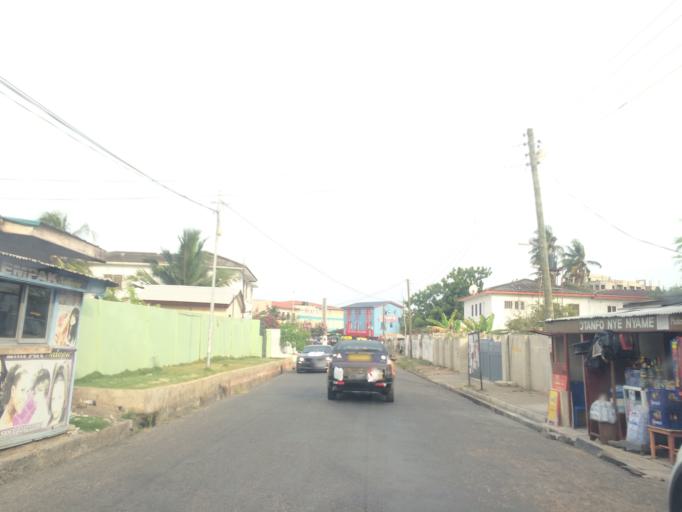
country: GH
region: Greater Accra
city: Accra
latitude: 5.5561
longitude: -0.1840
